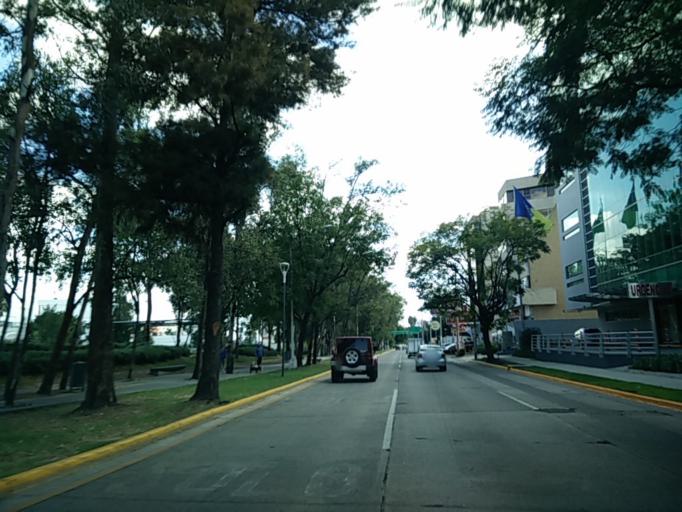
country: MX
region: Jalisco
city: Guadalajara
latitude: 20.6730
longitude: -103.4094
